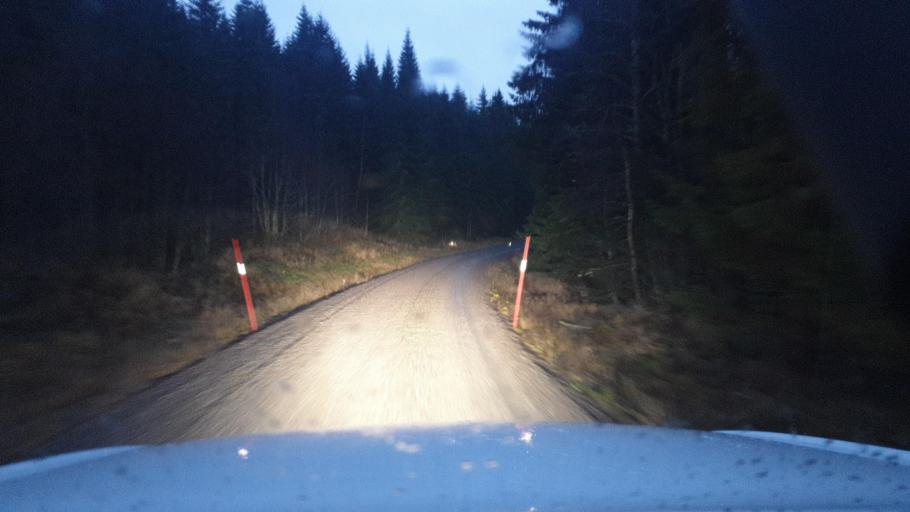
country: SE
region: Vaermland
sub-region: Eda Kommun
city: Charlottenberg
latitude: 60.0305
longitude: 12.6331
